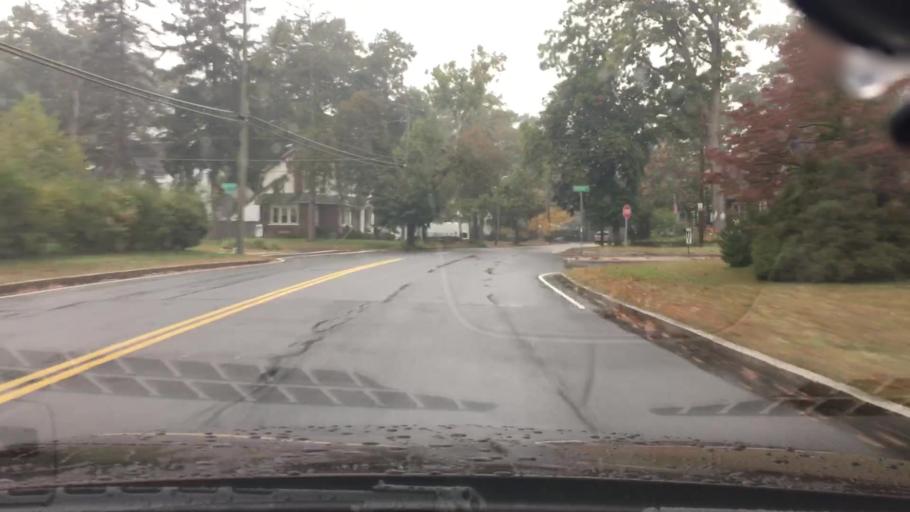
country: US
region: Massachusetts
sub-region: Hampden County
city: Longmeadow
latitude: 42.0763
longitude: -72.5535
